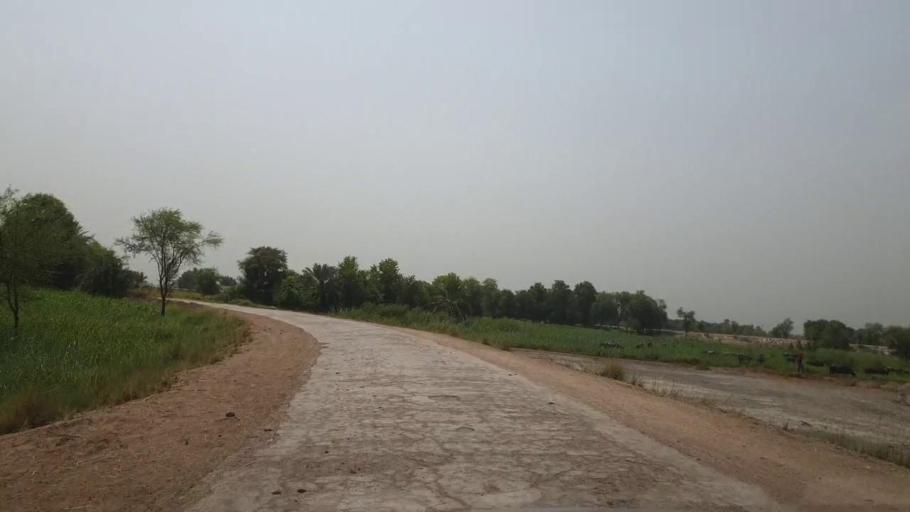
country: PK
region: Sindh
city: Gambat
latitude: 27.4427
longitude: 68.5156
